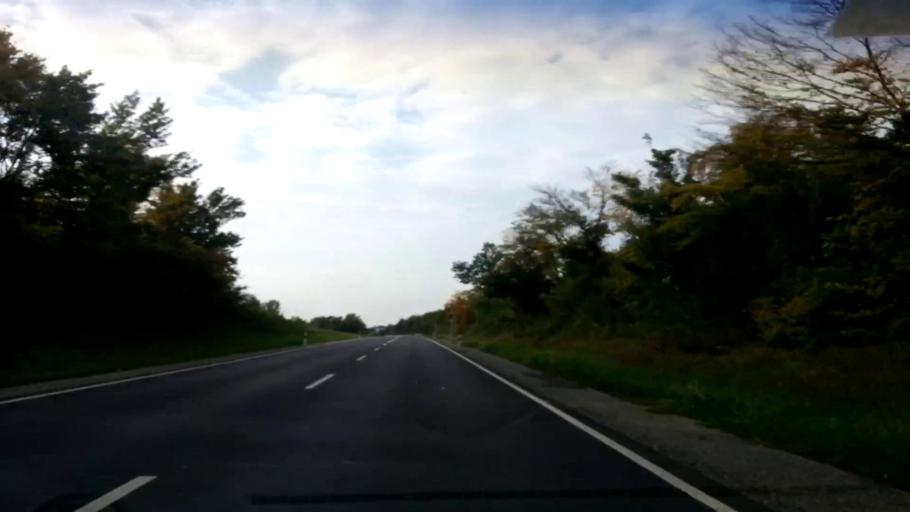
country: DE
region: Bavaria
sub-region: Regierungsbezirk Unterfranken
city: Gerolzhofen
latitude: 49.8939
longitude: 10.3588
